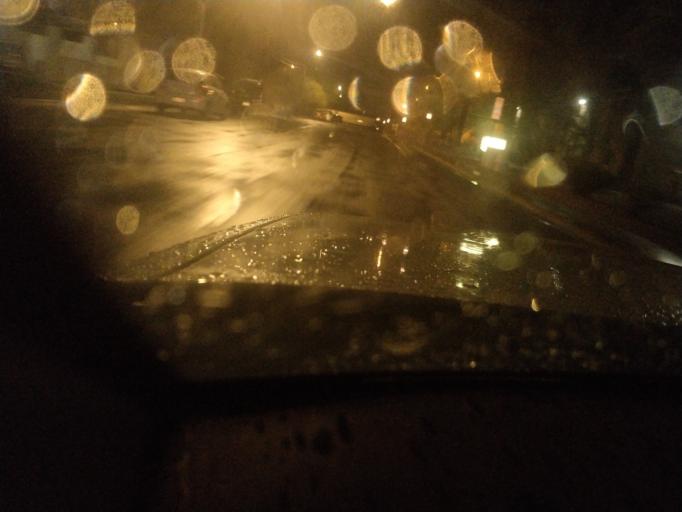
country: US
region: Arizona
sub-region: Maricopa County
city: Glendale
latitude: 33.5150
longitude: -112.1151
